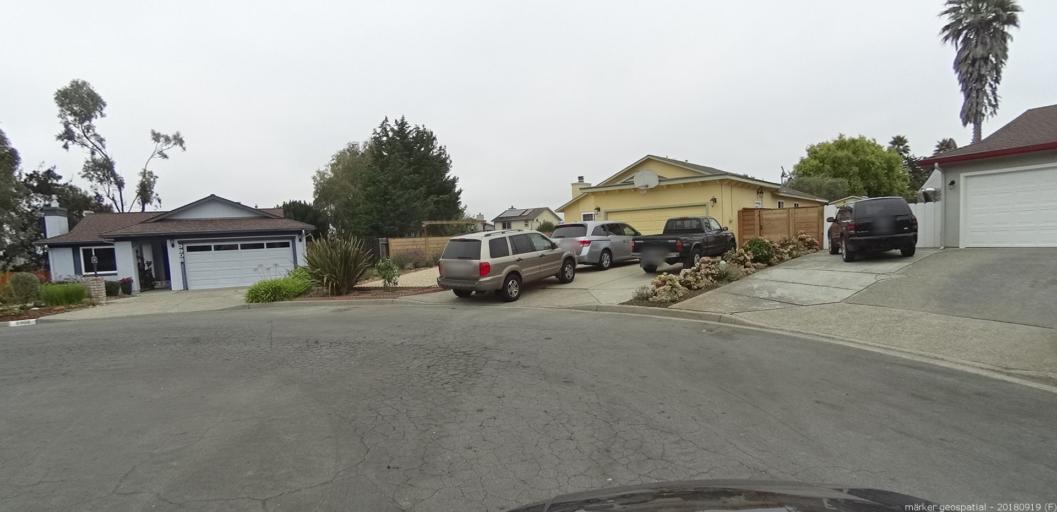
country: US
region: California
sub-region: Monterey County
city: Castroville
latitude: 36.7759
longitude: -121.7302
